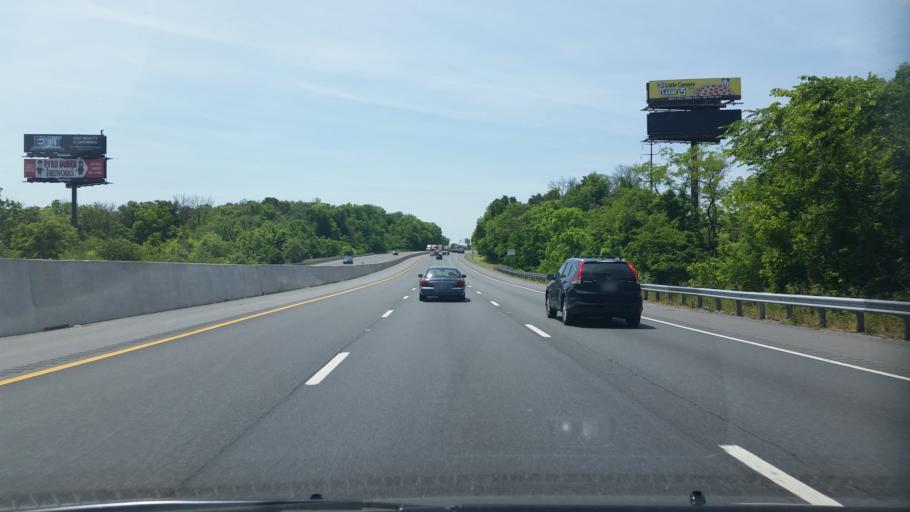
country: US
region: Maryland
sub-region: Washington County
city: Williamsport
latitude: 39.5711
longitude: -77.8871
